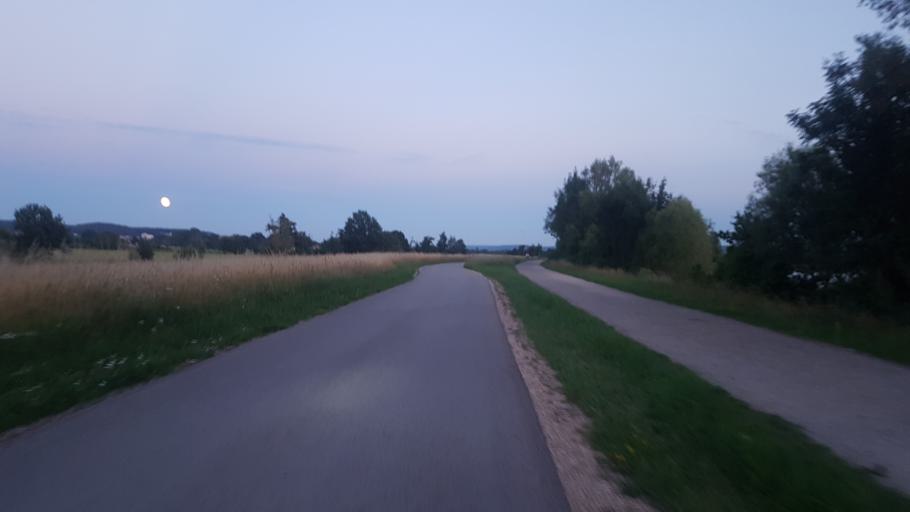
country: DE
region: Bavaria
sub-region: Regierungsbezirk Mittelfranken
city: Muhr am See
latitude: 49.1393
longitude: 10.7332
